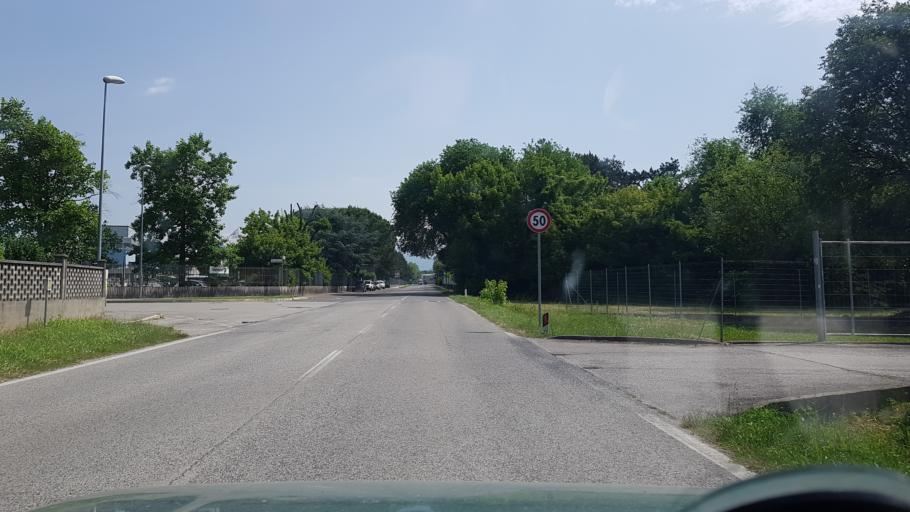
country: IT
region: Friuli Venezia Giulia
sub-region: Provincia di Gorizia
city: Savogna d'Isonzo
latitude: 45.9119
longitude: 13.5868
